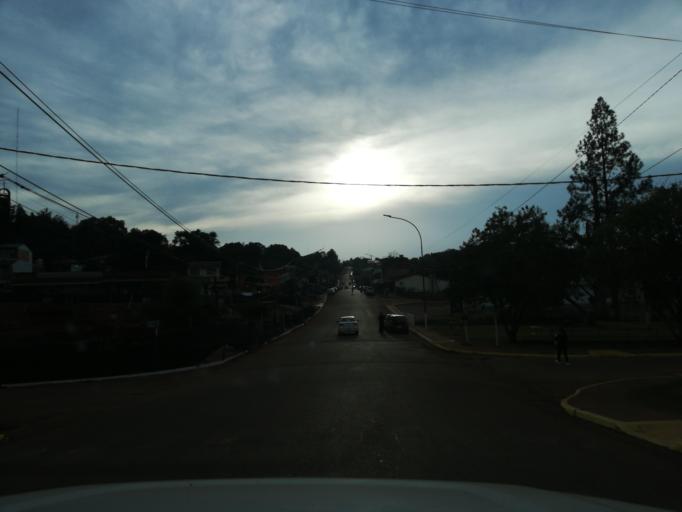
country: AR
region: Misiones
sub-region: Departamento de San Pedro
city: San Pedro
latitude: -26.6245
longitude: -54.1130
